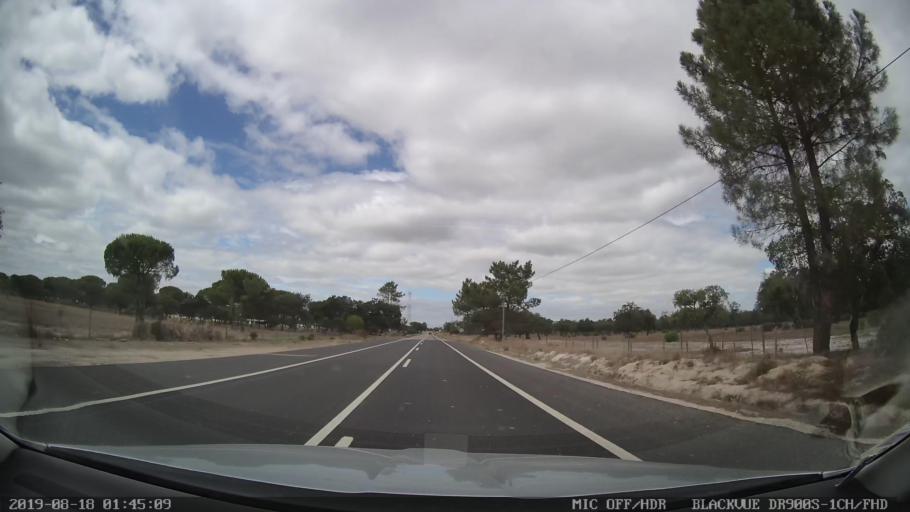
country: PT
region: Santarem
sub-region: Benavente
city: Benavente
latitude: 38.9151
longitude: -8.7682
